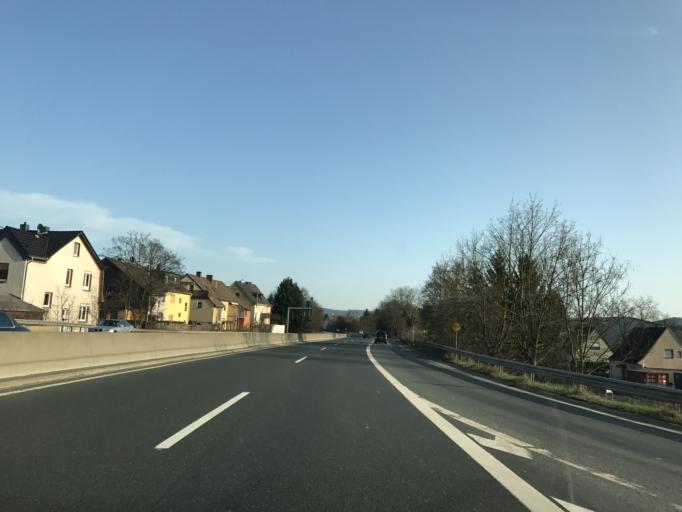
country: DE
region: Rheinland-Pfalz
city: Sankt Sebastian
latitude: 50.4207
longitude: 7.5671
